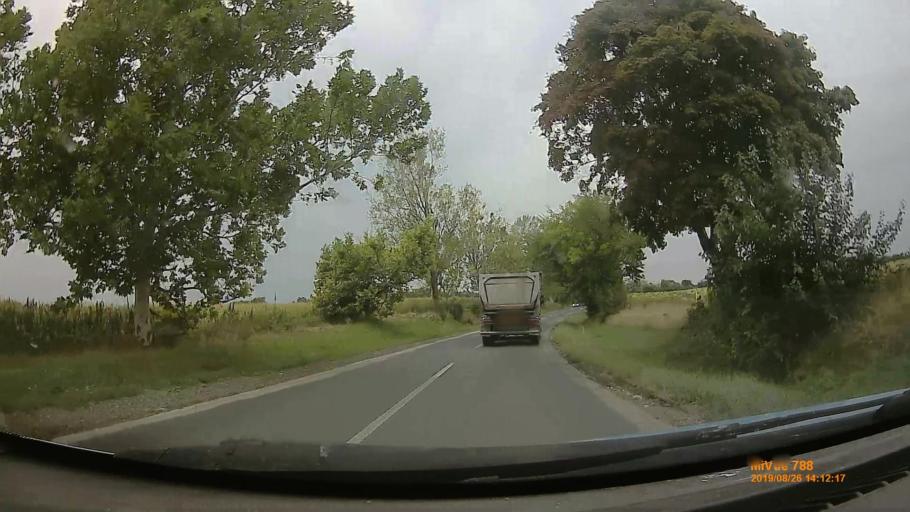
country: HU
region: Fejer
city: Szarliget
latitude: 47.4399
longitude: 18.5379
